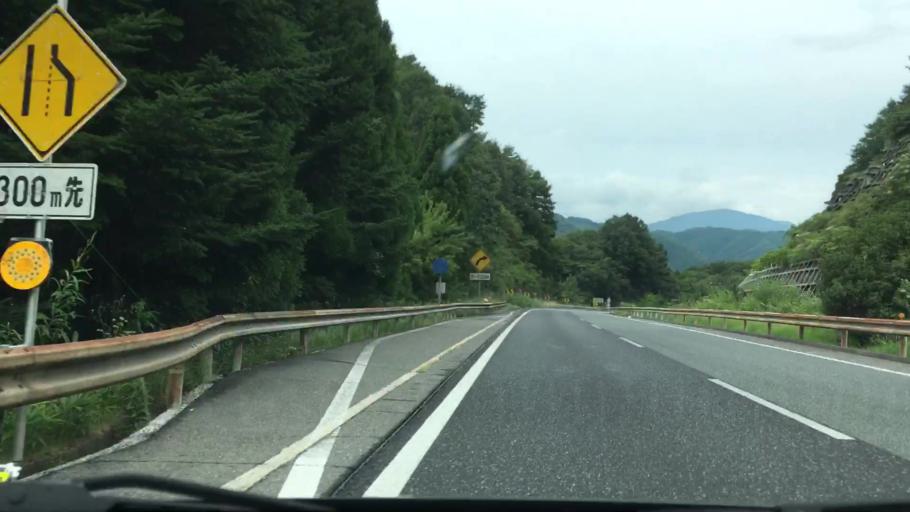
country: JP
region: Okayama
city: Niimi
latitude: 35.0138
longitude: 133.5857
